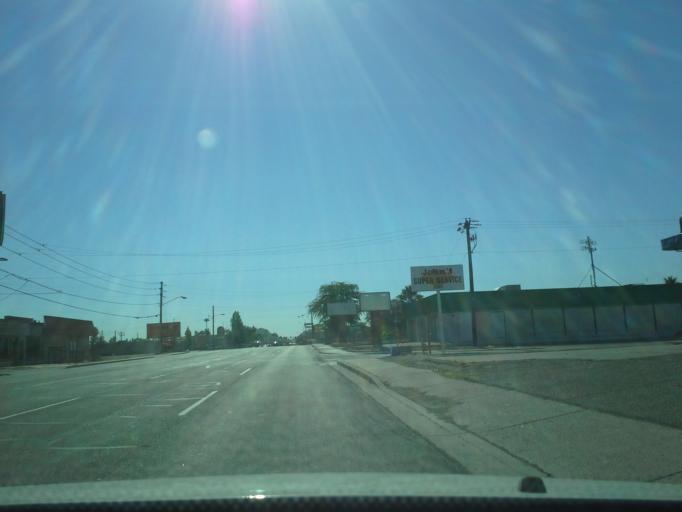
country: US
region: Arizona
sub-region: Maricopa County
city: Phoenix
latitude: 33.4657
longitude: -112.0178
